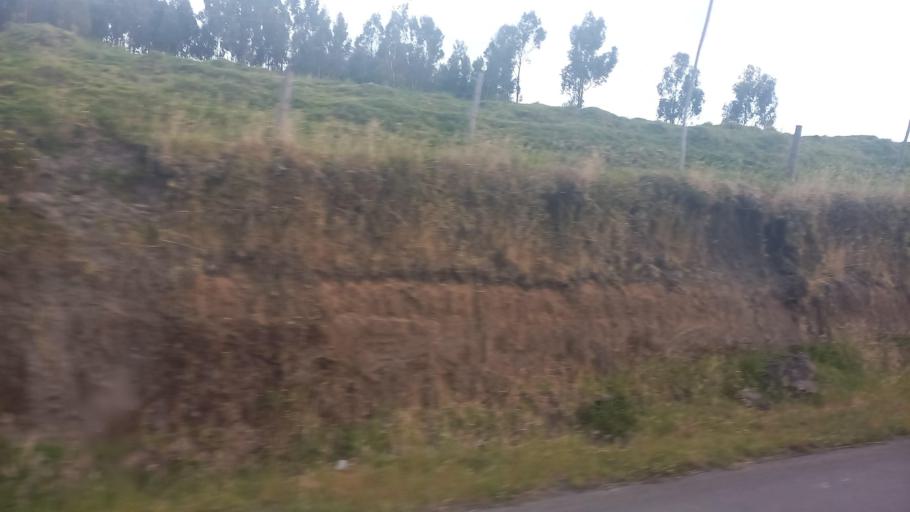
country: EC
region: Pichincha
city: Cayambe
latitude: 0.1024
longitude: -78.0850
